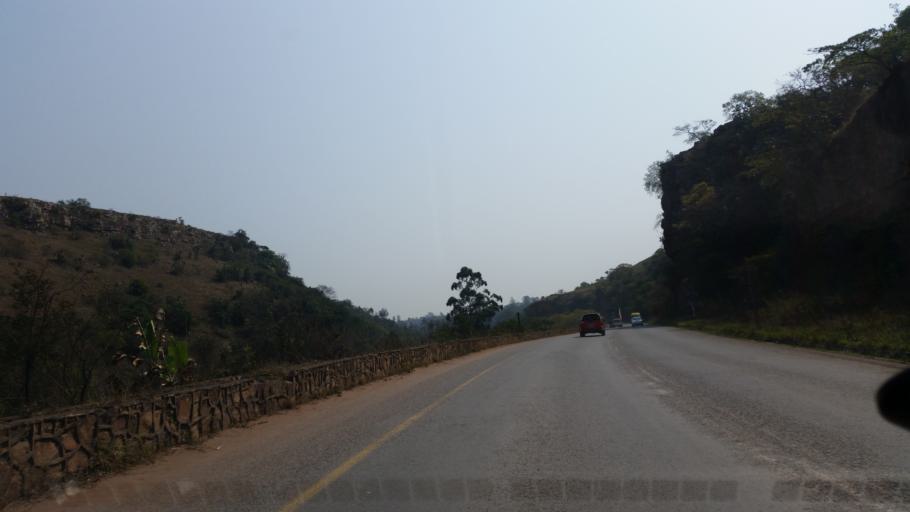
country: ZA
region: KwaZulu-Natal
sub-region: eThekwini Metropolitan Municipality
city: Mpumalanga
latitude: -29.7541
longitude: 30.6657
